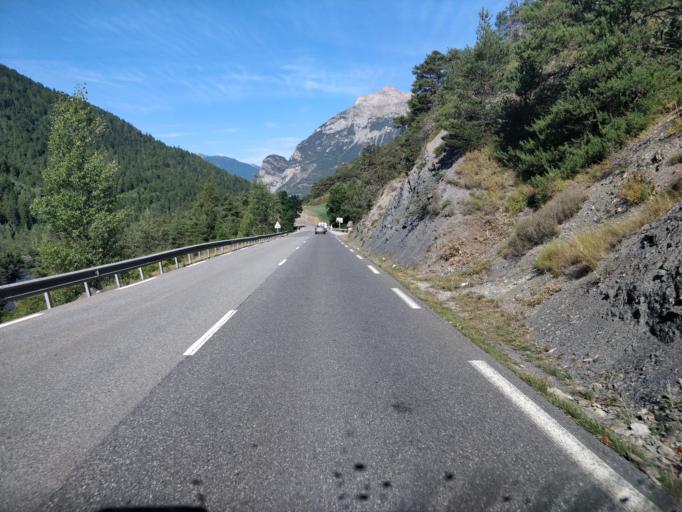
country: FR
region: Provence-Alpes-Cote d'Azur
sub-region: Departement des Alpes-de-Haute-Provence
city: Barcelonnette
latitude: 44.3933
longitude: 6.5553
